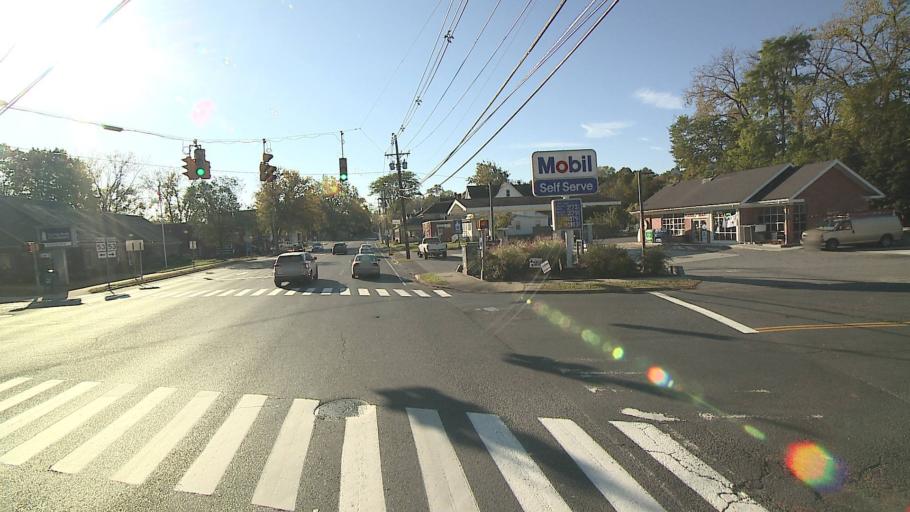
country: US
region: Connecticut
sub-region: Fairfield County
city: Bethel
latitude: 41.3762
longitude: -73.4251
